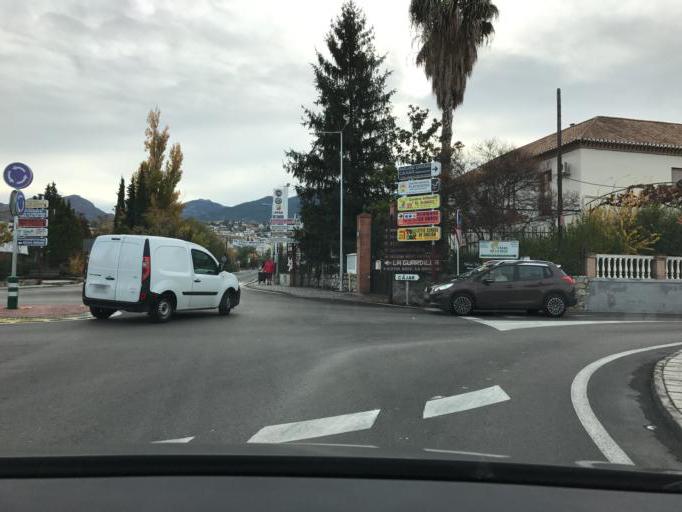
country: ES
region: Andalusia
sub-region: Provincia de Granada
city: Huetor Vega
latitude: 37.1401
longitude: -3.5702
